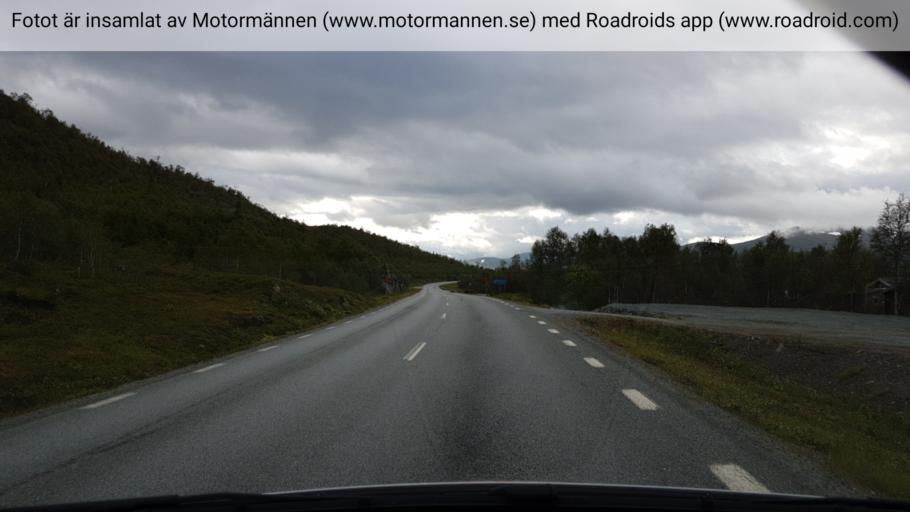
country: NO
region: Nordland
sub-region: Rana
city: Mo i Rana
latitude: 66.1333
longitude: 14.5954
